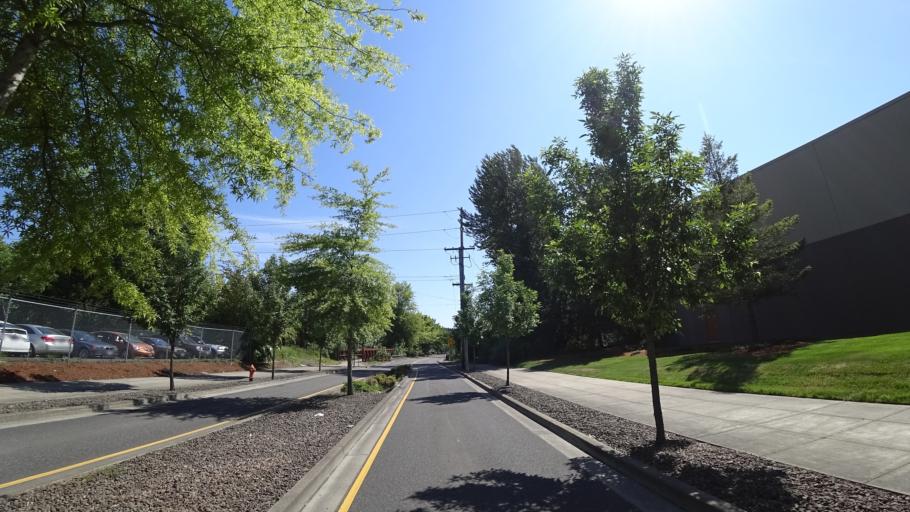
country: US
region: Oregon
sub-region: Multnomah County
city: Lents
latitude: 45.5692
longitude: -122.5673
